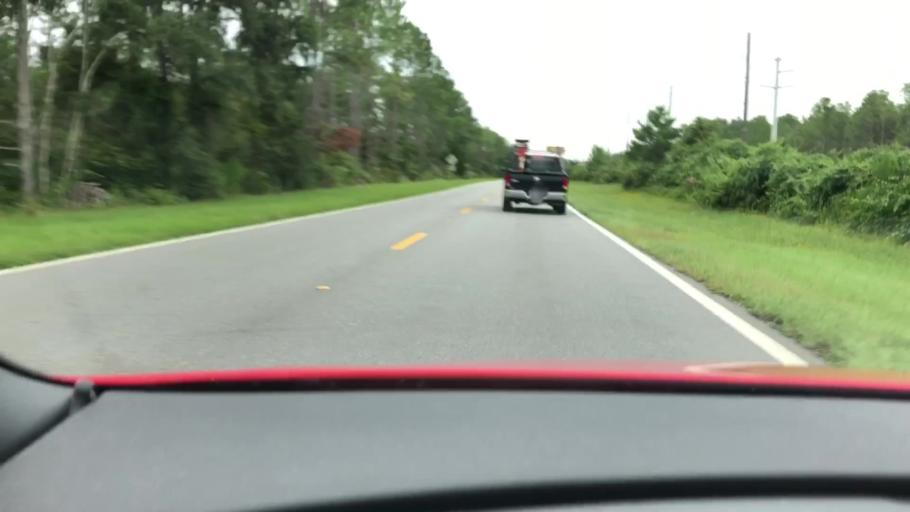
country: US
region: Florida
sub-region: Flagler County
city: Palm Coast
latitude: 29.5249
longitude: -81.2006
